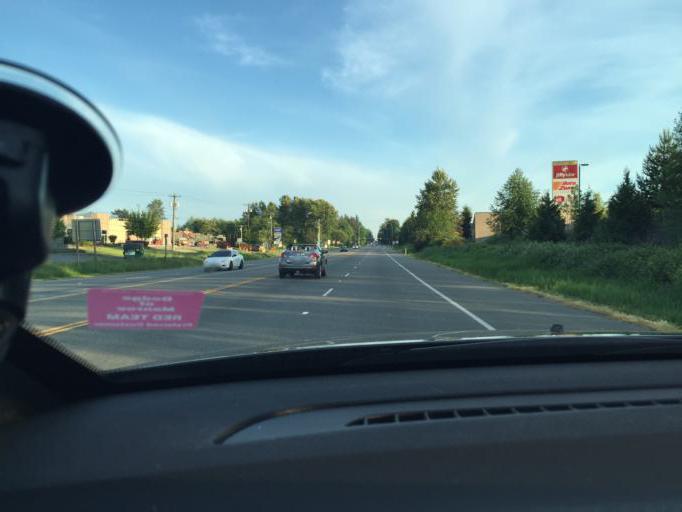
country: US
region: Washington
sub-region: Snohomish County
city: West Lake Stevens
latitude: 48.0021
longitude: -122.1063
